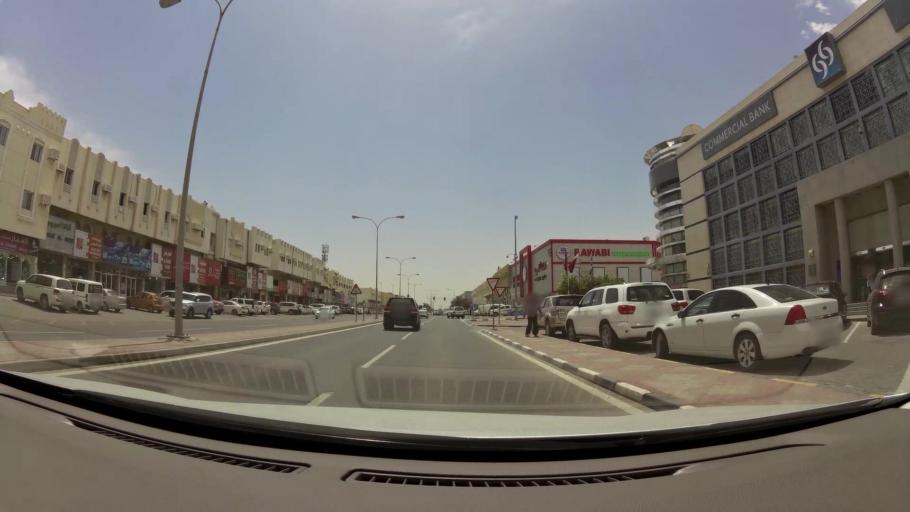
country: QA
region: Baladiyat ar Rayyan
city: Ar Rayyan
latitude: 25.2910
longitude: 51.4201
